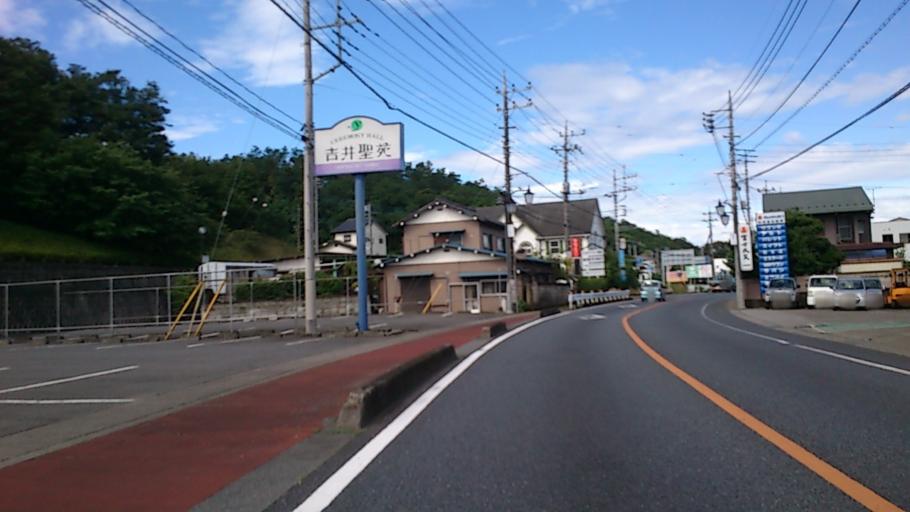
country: JP
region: Gunma
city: Yoshii
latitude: 36.2509
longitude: 138.9784
